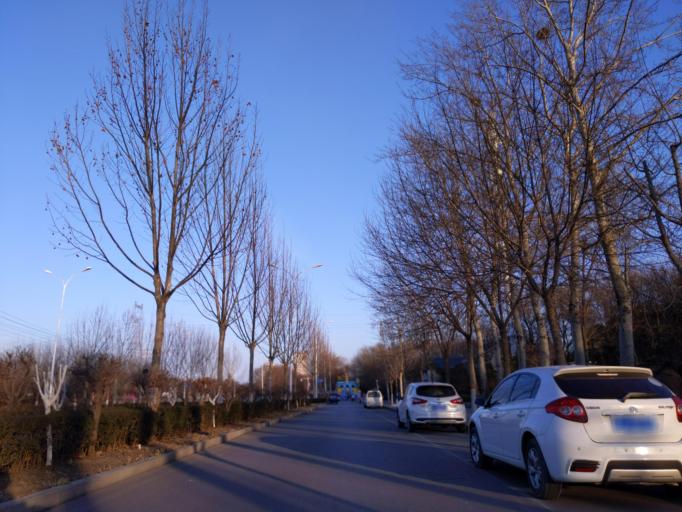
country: CN
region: Henan Sheng
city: Puyang
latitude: 35.7659
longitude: 114.9996
